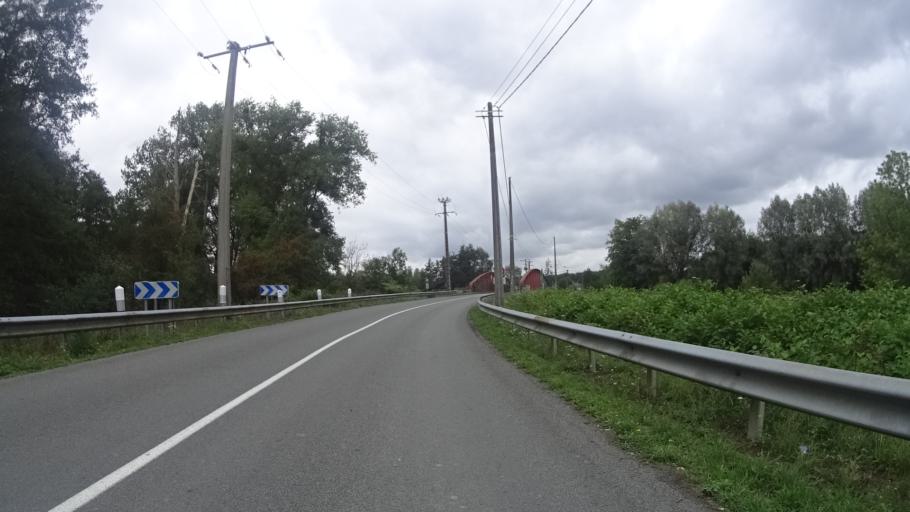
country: FR
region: Nord-Pas-de-Calais
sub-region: Departement du Nord
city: Maroilles
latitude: 50.1556
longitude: 3.7440
